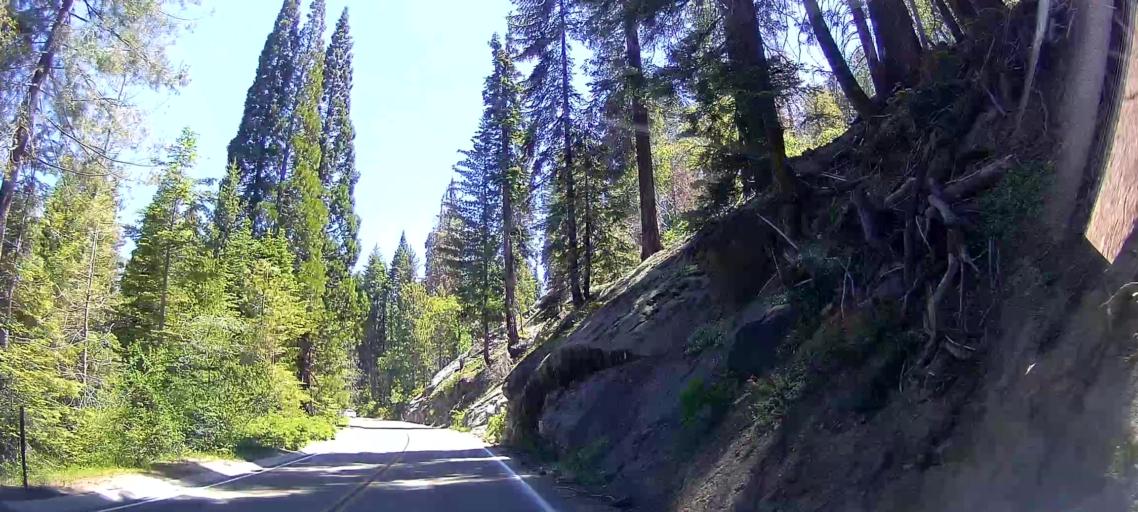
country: US
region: California
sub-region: Tulare County
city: Three Rivers
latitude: 36.5732
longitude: -118.7634
